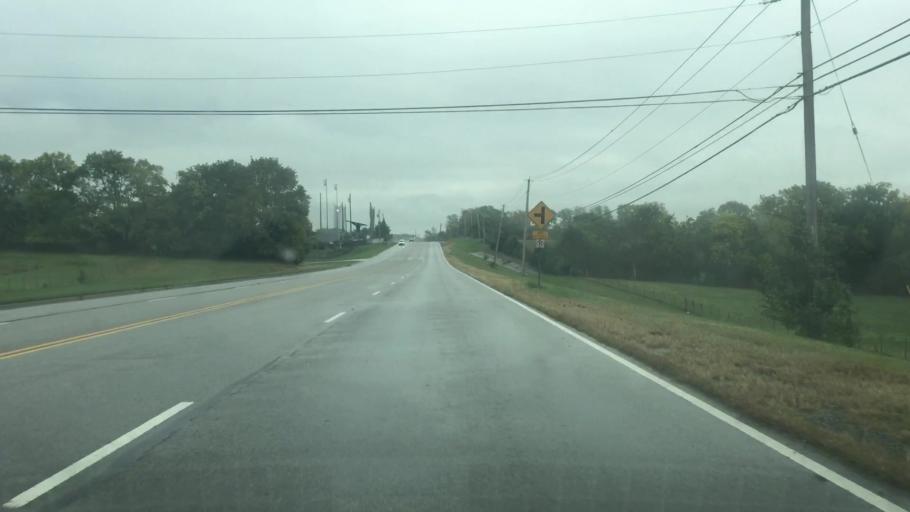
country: US
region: Kansas
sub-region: Johnson County
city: Lenexa
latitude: 38.9709
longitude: -94.8036
